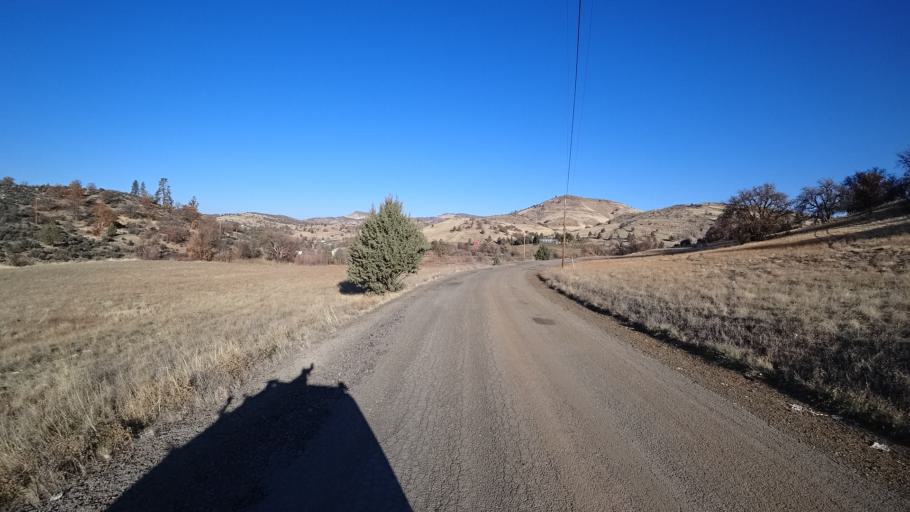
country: US
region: California
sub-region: Siskiyou County
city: Montague
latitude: 41.8950
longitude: -122.4943
